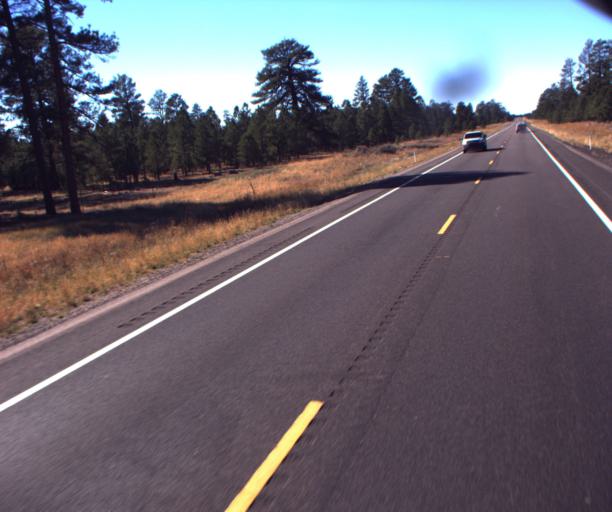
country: US
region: Arizona
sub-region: Apache County
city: Saint Michaels
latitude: 35.6985
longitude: -109.2832
